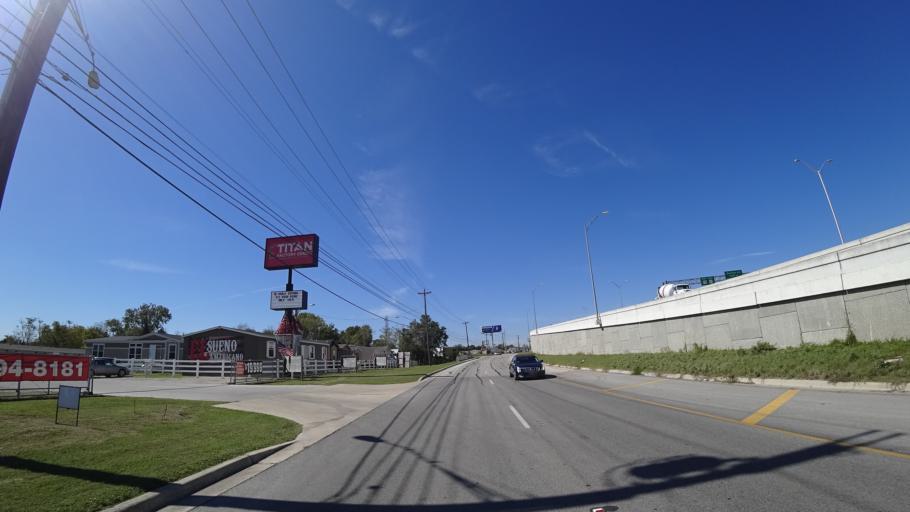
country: US
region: Texas
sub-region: Travis County
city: Austin
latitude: 30.2124
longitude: -97.7083
